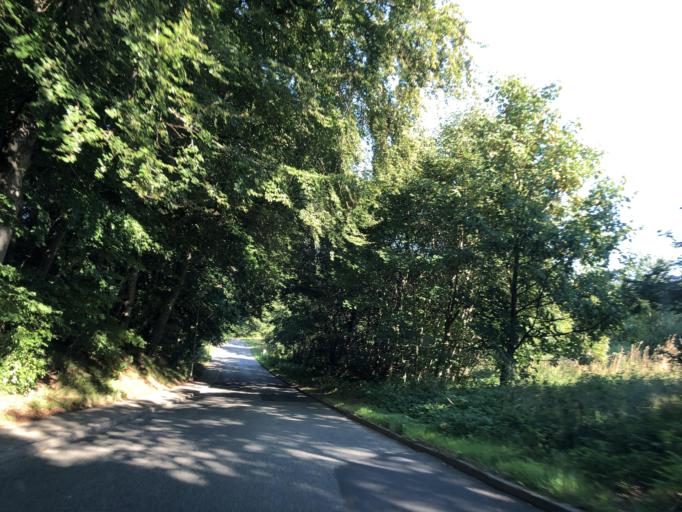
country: DK
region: North Denmark
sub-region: Mariagerfjord Kommune
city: Hobro
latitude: 56.6336
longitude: 9.8201
